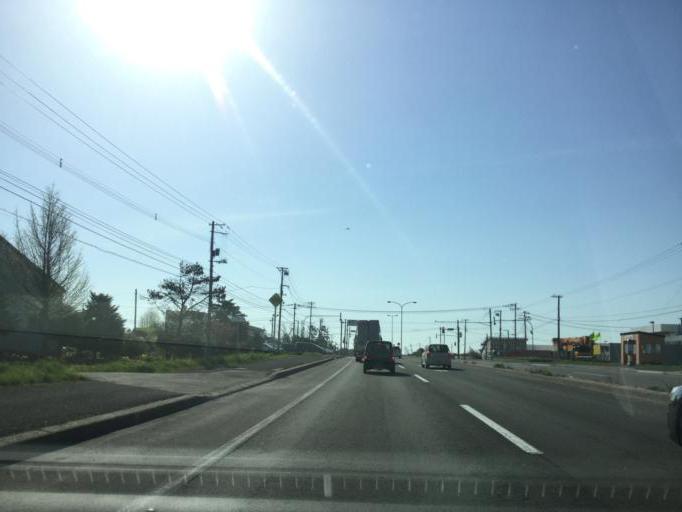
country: JP
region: Hokkaido
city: Kitahiroshima
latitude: 43.0063
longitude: 141.5244
